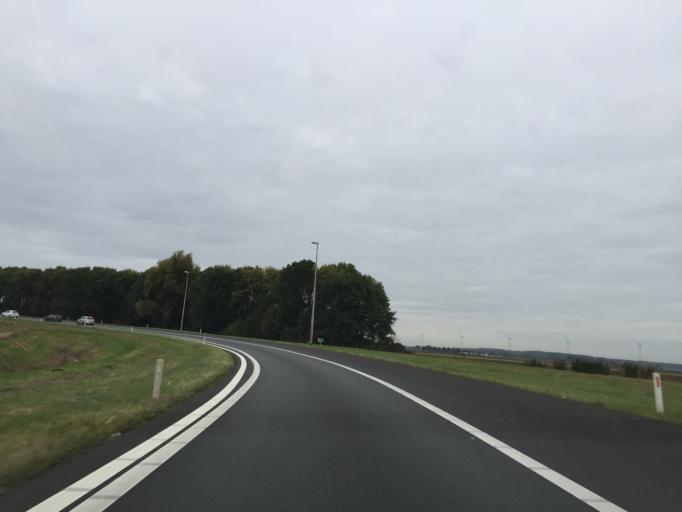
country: NL
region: North Brabant
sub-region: Gemeente Breda
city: Breda
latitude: 51.6468
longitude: 4.6880
